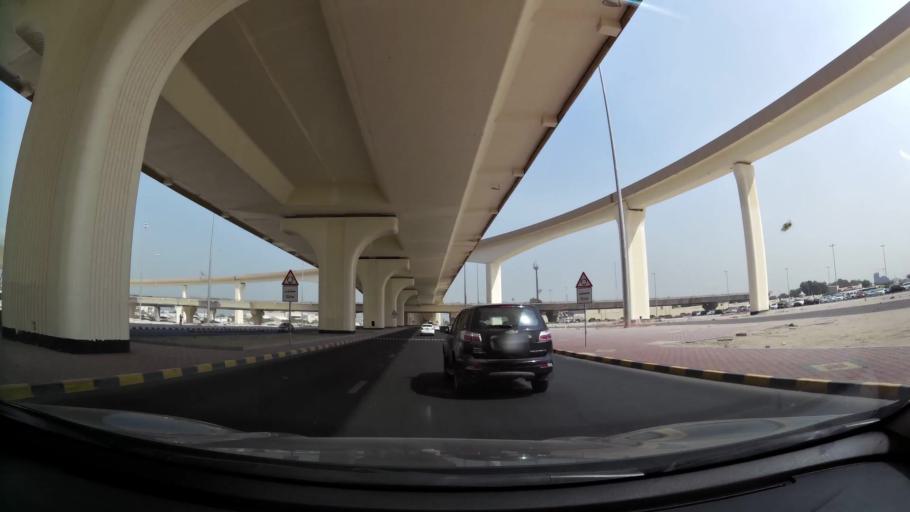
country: KW
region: Al Asimah
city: Ar Rabiyah
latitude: 29.3165
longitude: 47.8982
